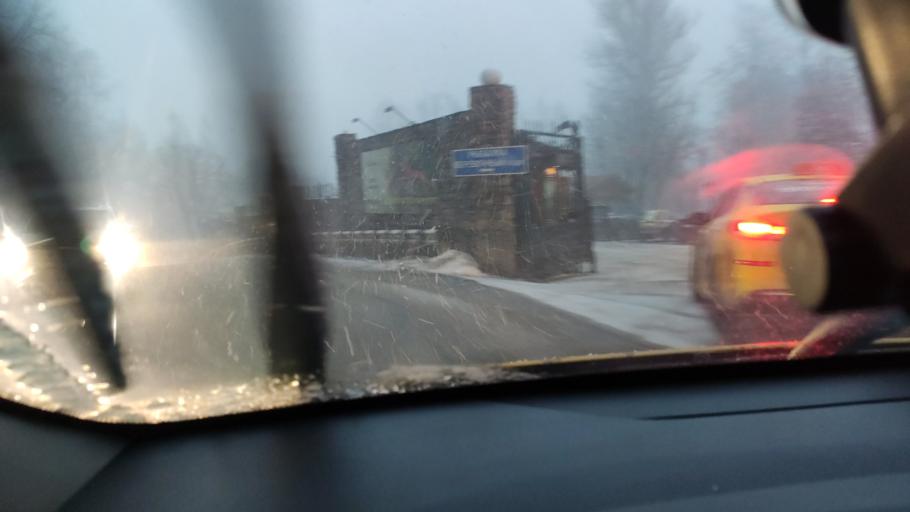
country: RU
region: Moskovskaya
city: Biryulevo Zapadnoye
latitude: 55.5608
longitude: 37.6405
